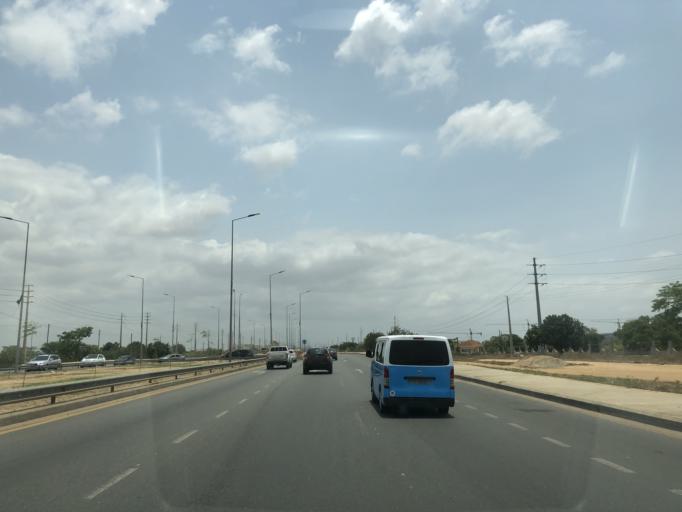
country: AO
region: Luanda
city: Luanda
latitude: -8.9462
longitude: 13.2600
